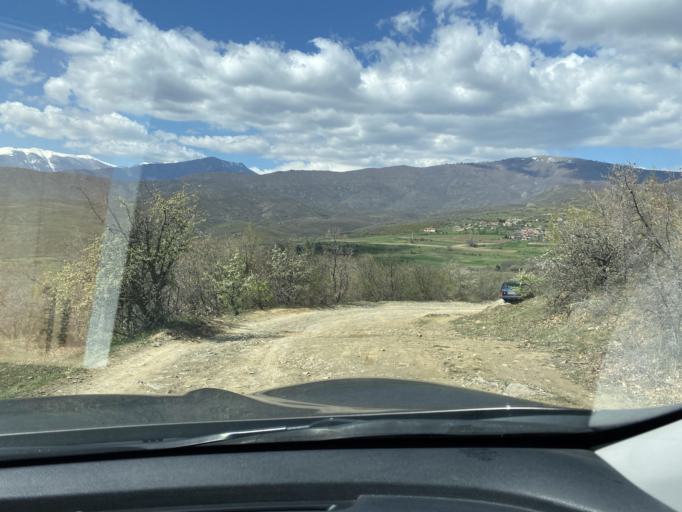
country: MK
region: Caska
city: Caska
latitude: 41.7310
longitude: 21.6553
